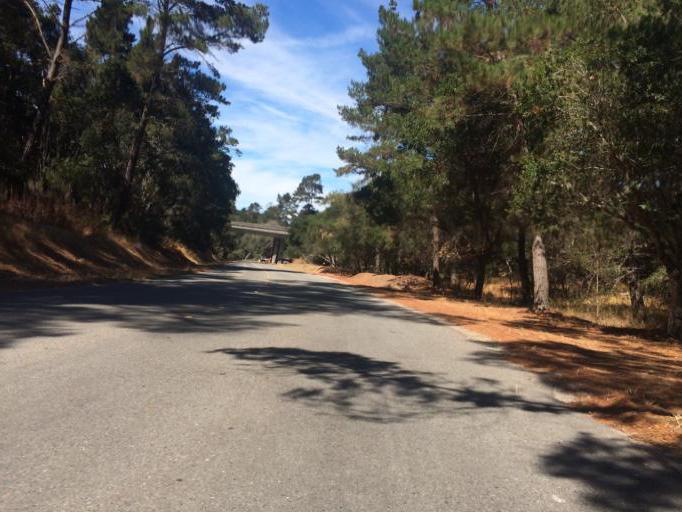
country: US
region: California
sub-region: Monterey County
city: Monterey
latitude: 36.5820
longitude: -121.8914
